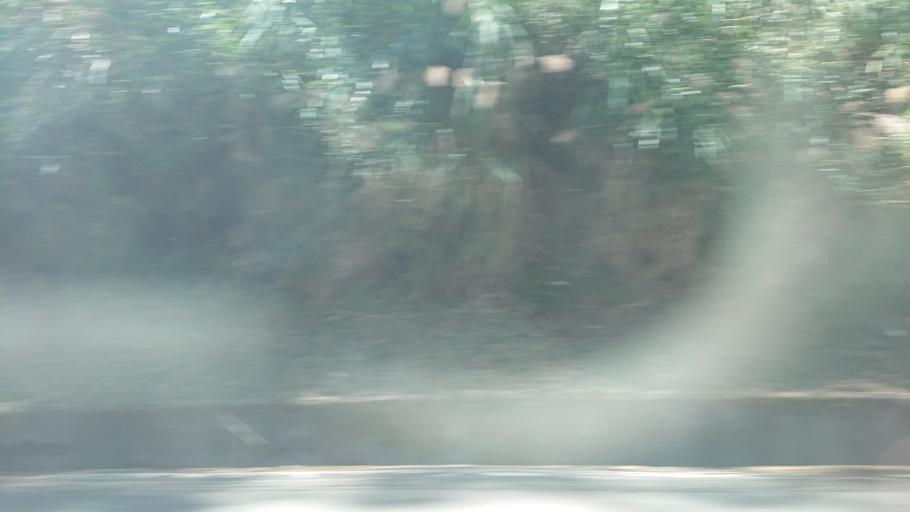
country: TW
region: Taiwan
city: Lugu
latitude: 23.4737
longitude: 120.8476
